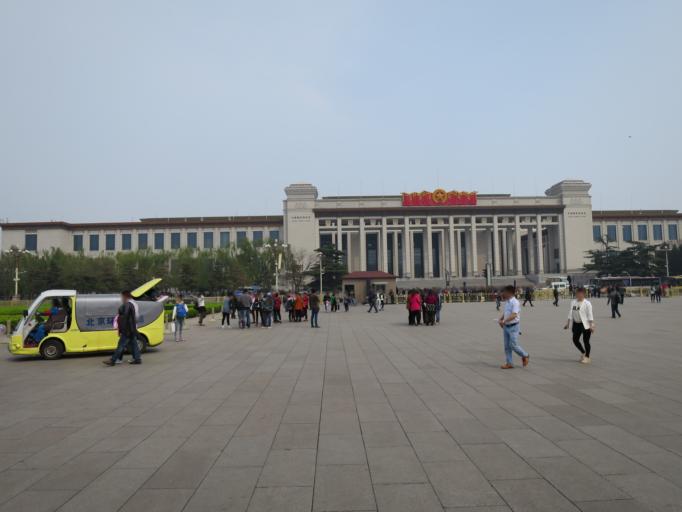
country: CN
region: Beijing
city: Beijing
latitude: 39.9040
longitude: 116.3923
